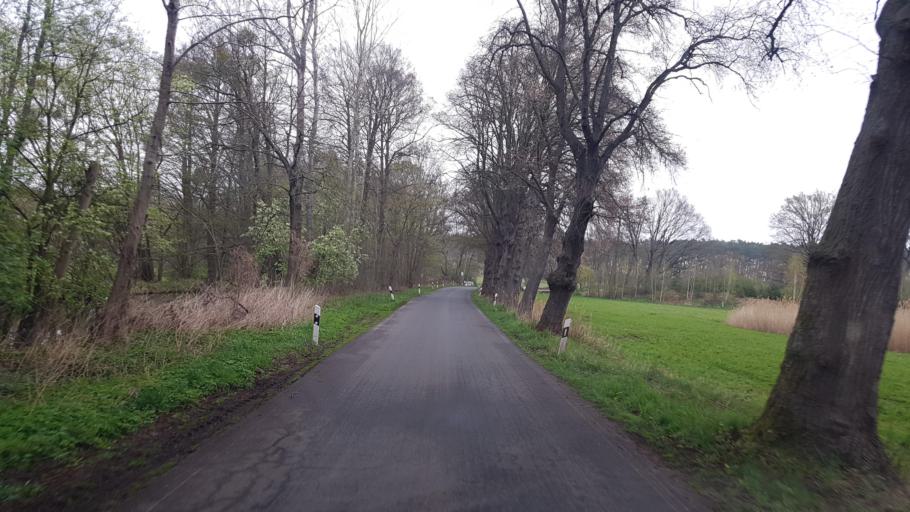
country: DE
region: Brandenburg
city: Drahnsdorf
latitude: 51.9017
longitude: 13.5510
